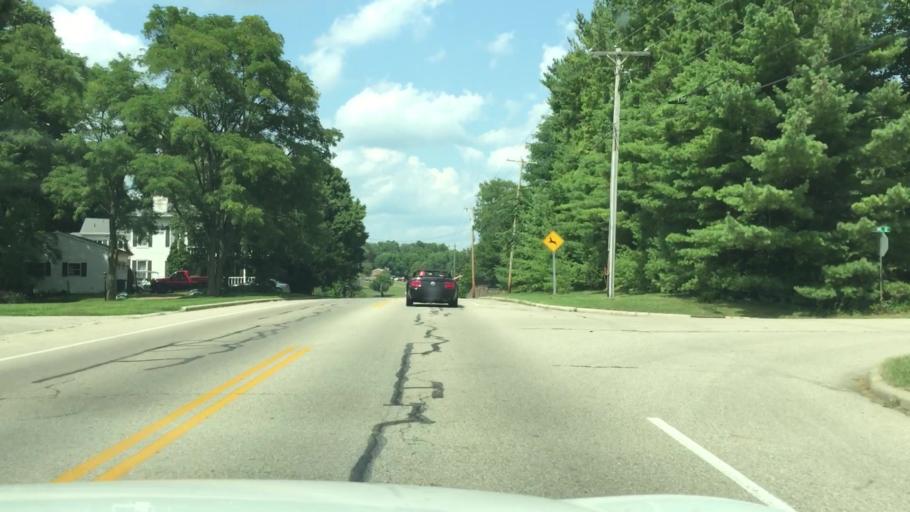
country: US
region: Ohio
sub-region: Clark County
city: Northridge
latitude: 39.9323
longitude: -83.7335
